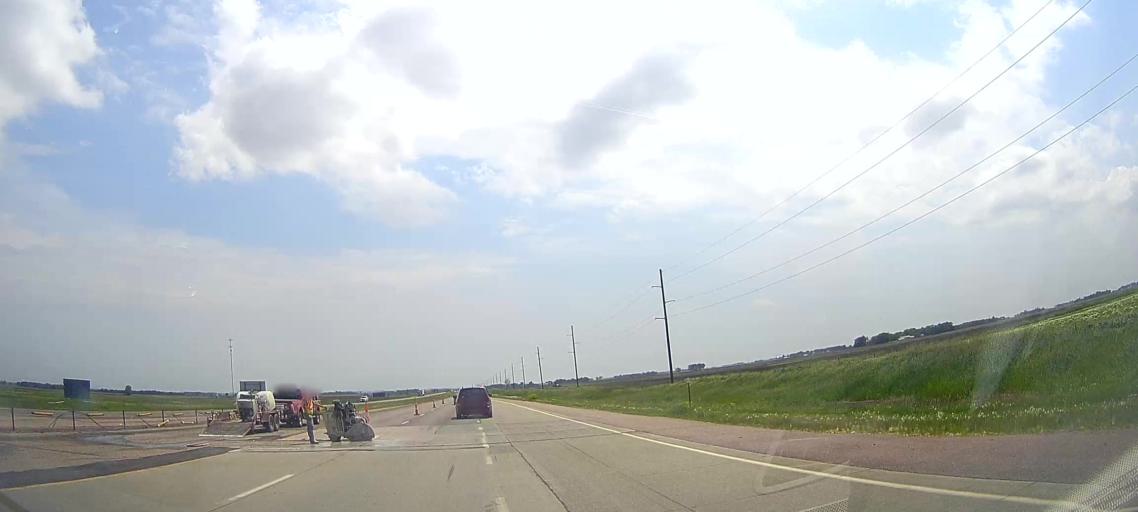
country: US
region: South Dakota
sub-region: Lincoln County
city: Lennox
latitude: 43.2947
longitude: -96.7965
